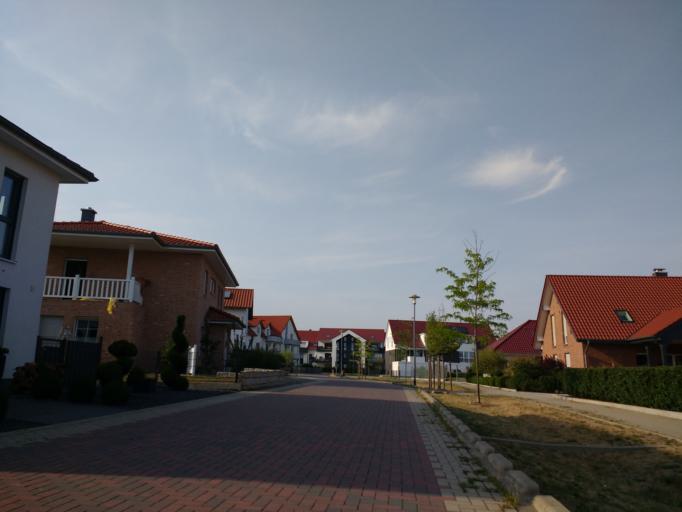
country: DE
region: Lower Saxony
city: Gifhorn
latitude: 52.4961
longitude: 10.5345
